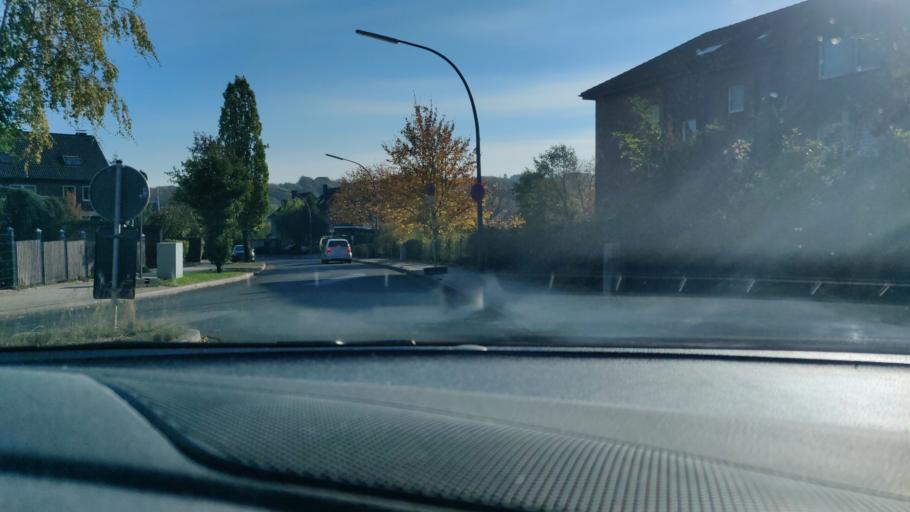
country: DE
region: North Rhine-Westphalia
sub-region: Regierungsbezirk Dusseldorf
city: Velbert
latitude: 51.3470
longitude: 7.0152
